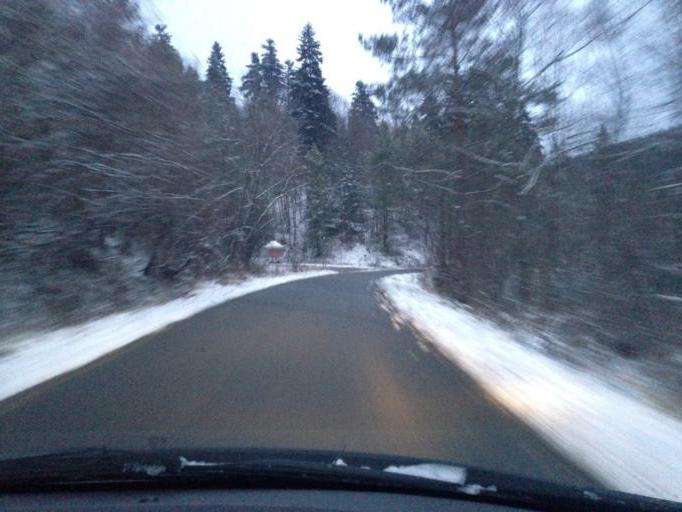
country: PL
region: Subcarpathian Voivodeship
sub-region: Powiat jasielski
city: Krempna
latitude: 49.5063
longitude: 21.5370
